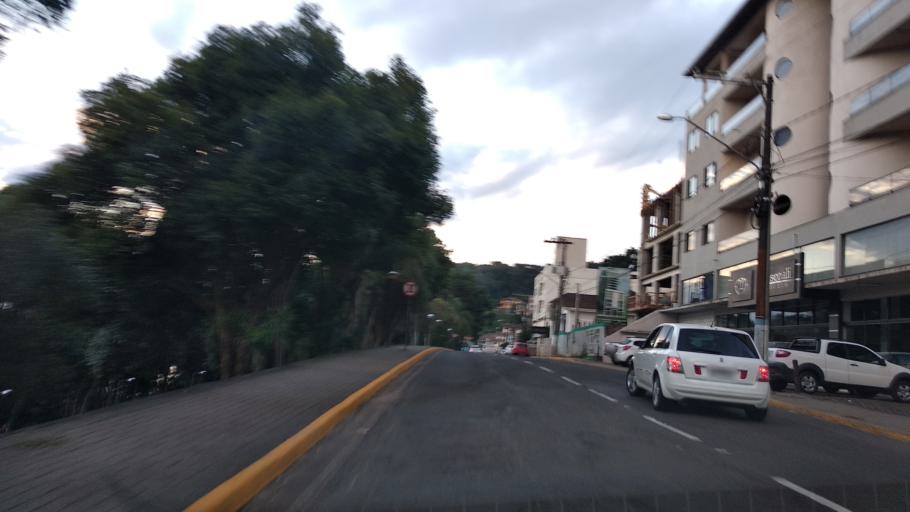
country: BR
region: Santa Catarina
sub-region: Videira
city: Videira
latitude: -27.0029
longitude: -51.1558
